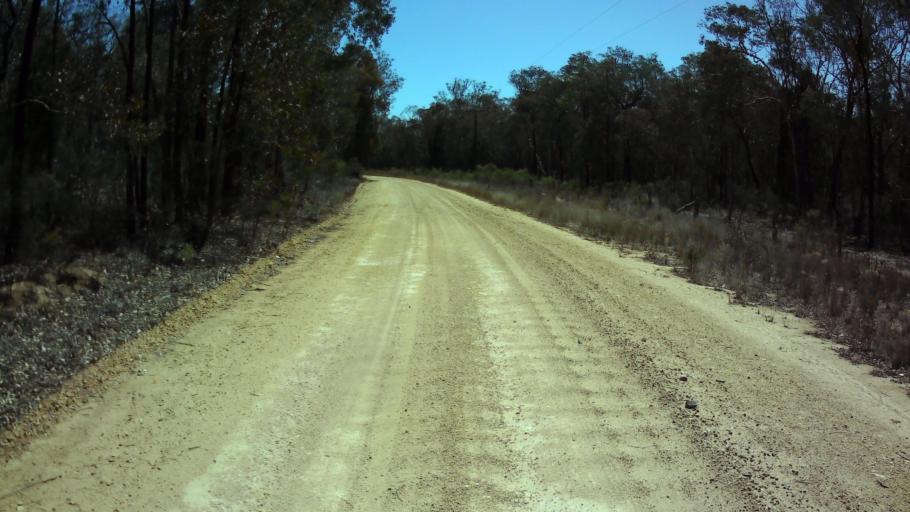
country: AU
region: New South Wales
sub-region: Cowra
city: Cowra
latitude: -33.8425
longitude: 148.4518
